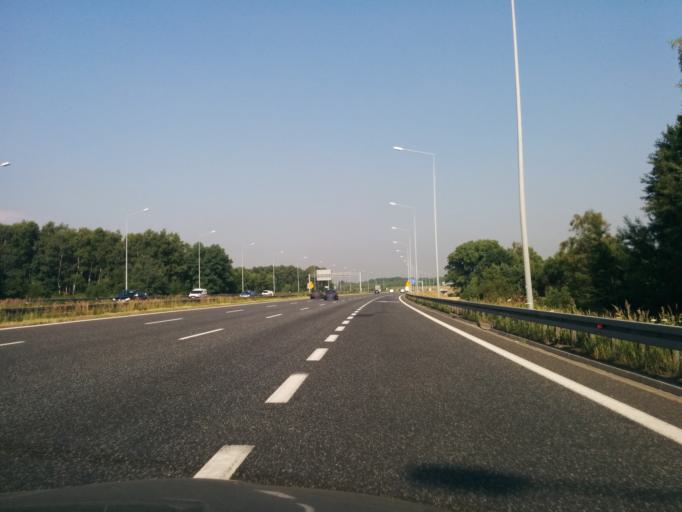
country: PL
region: Silesian Voivodeship
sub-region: Powiat gliwicki
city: Paniowki
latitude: 50.2618
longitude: 18.7915
